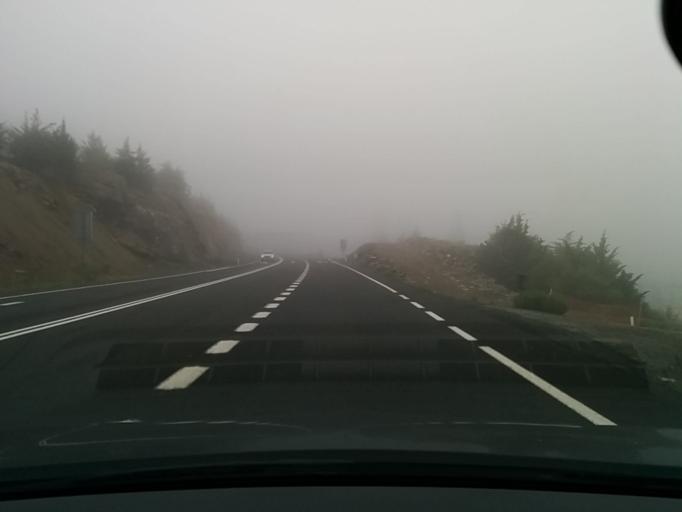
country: ES
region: Aragon
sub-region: Provincia de Huesca
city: Arguis
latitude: 42.3444
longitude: -0.3935
